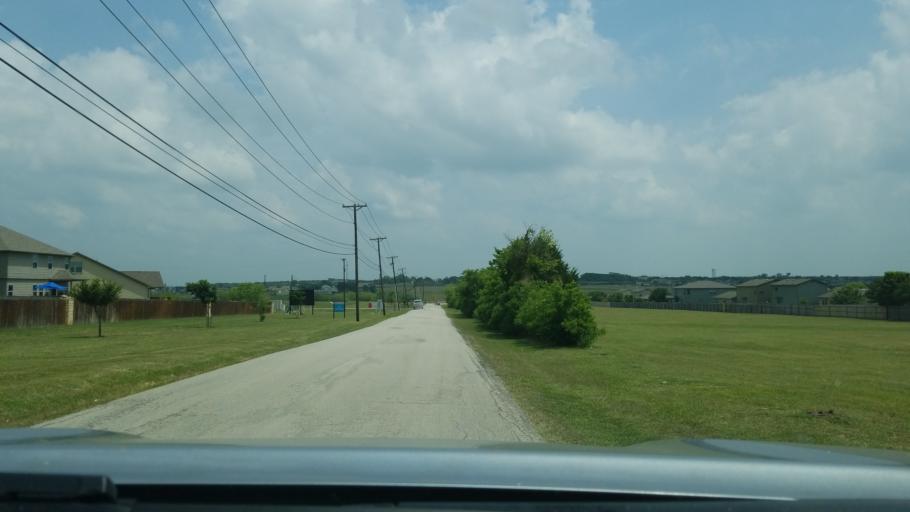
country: US
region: Texas
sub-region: Comal County
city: New Braunfels
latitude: 29.7596
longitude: -98.0672
